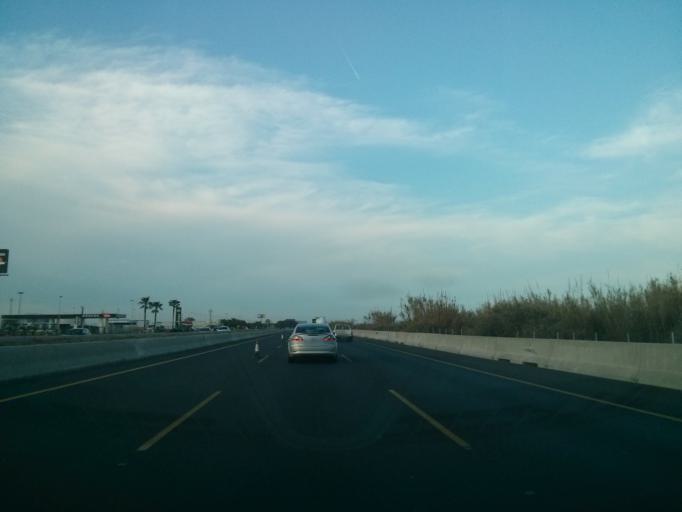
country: ES
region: Valencia
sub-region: Provincia de Valencia
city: Meliana
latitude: 39.5284
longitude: -0.3131
